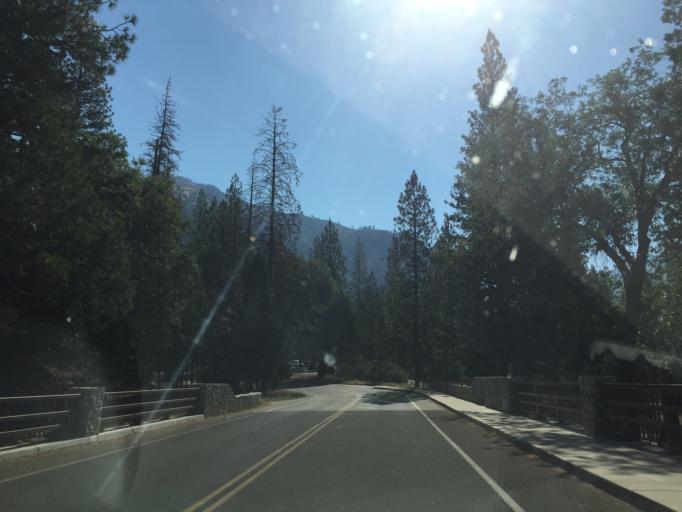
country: US
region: California
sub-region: Tulare County
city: Three Rivers
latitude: 36.7899
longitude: -118.6698
